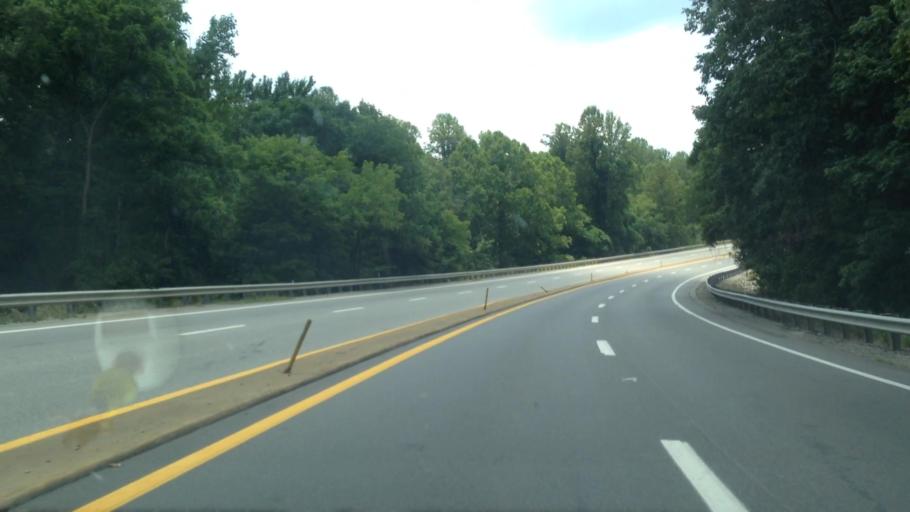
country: US
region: Virginia
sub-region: Henry County
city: Chatmoss
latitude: 36.5825
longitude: -79.8622
